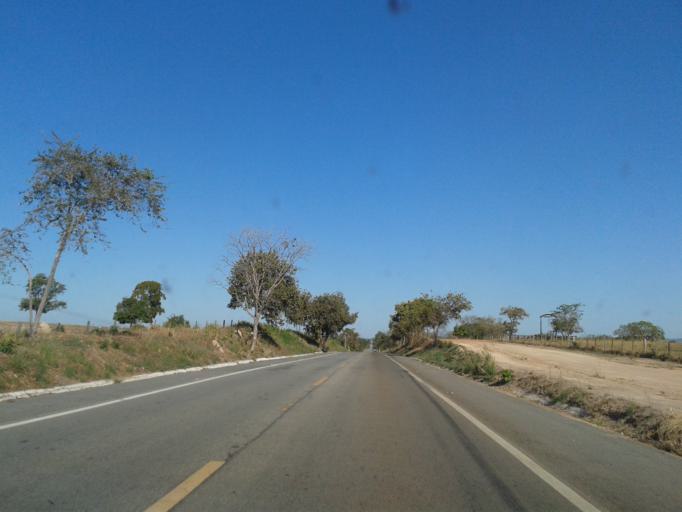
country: BR
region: Goias
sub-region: Mozarlandia
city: Mozarlandia
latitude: -15.2635
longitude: -50.4897
